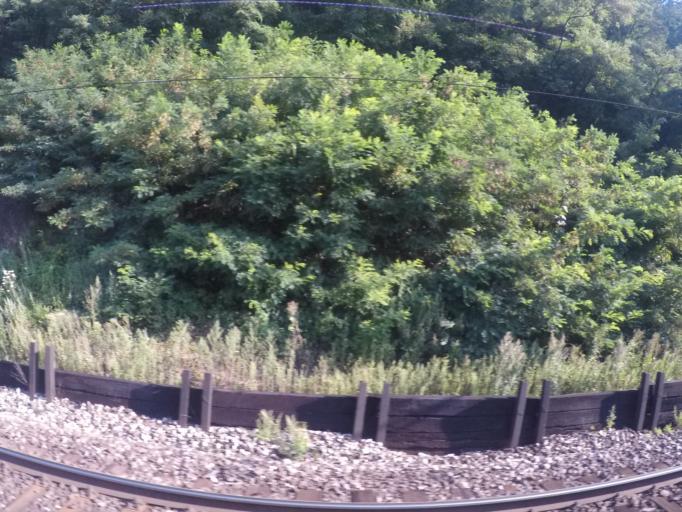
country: SK
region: Kosicky
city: Gelnica
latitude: 48.8933
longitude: 21.0268
